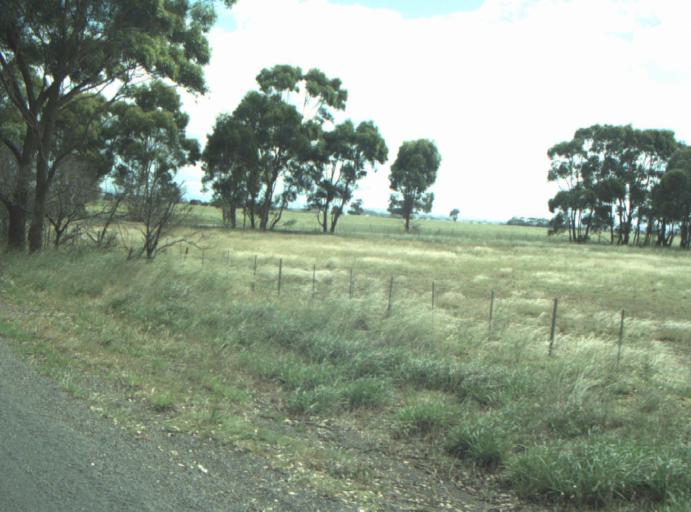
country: AU
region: Victoria
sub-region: Greater Geelong
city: Lara
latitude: -37.8710
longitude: 144.3501
